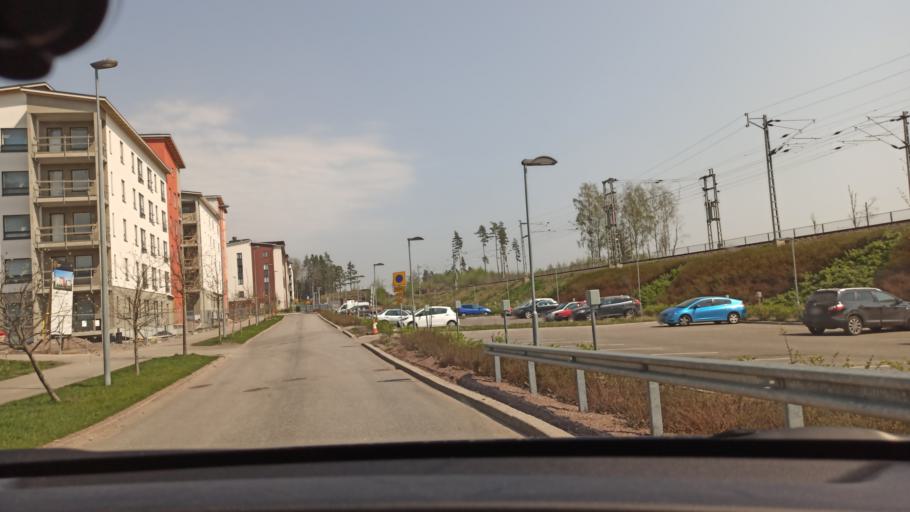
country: FI
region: Uusimaa
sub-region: Helsinki
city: Kirkkonummi
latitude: 60.1197
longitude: 24.4745
